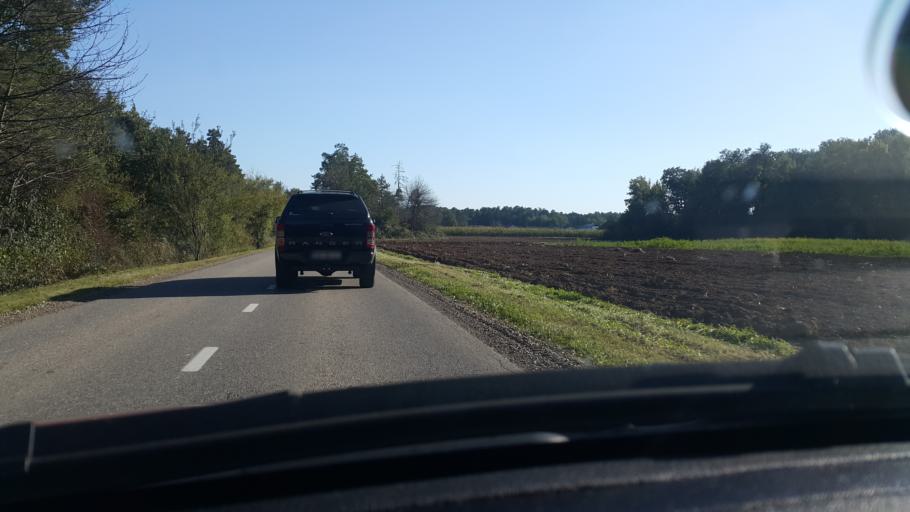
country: SI
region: Race-Fram
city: Race
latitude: 46.4716
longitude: 15.7107
